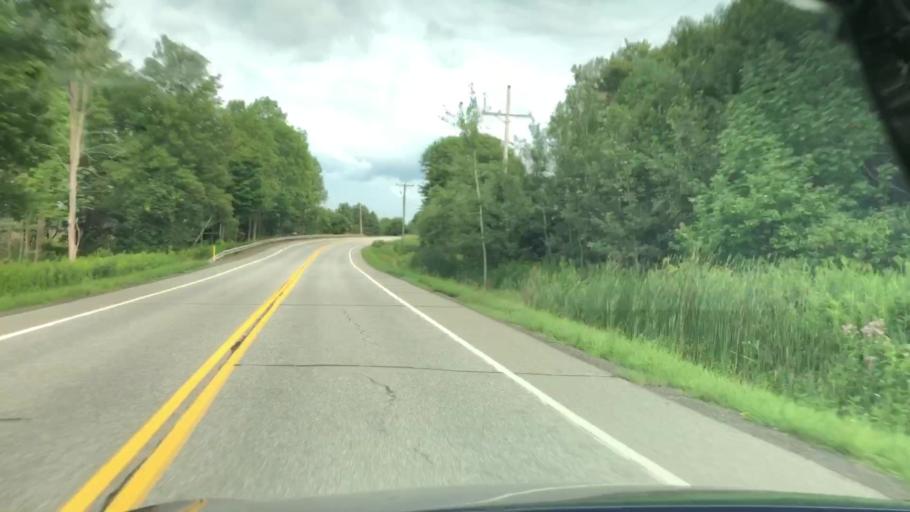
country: US
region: Pennsylvania
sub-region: Erie County
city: Northwest Harborcreek
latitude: 42.0608
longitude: -79.8715
